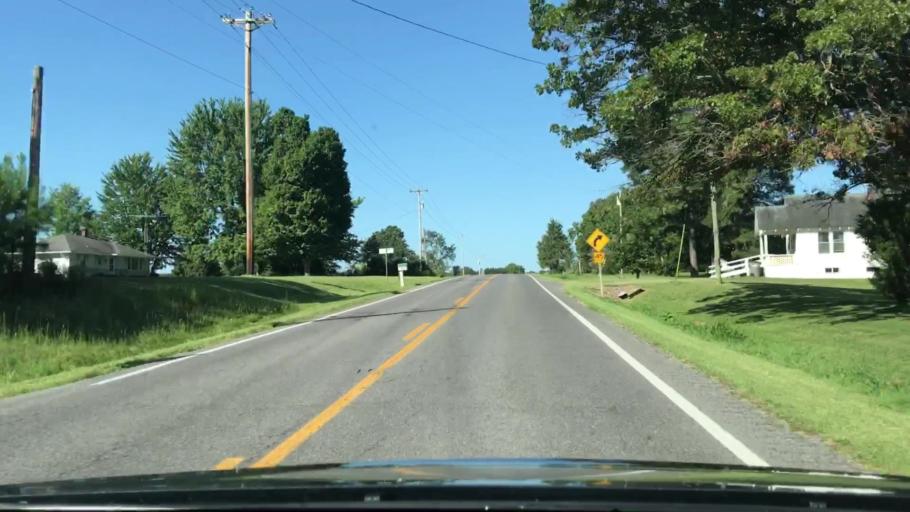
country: US
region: Kentucky
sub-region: Graves County
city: Mayfield
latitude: 36.7740
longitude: -88.4960
